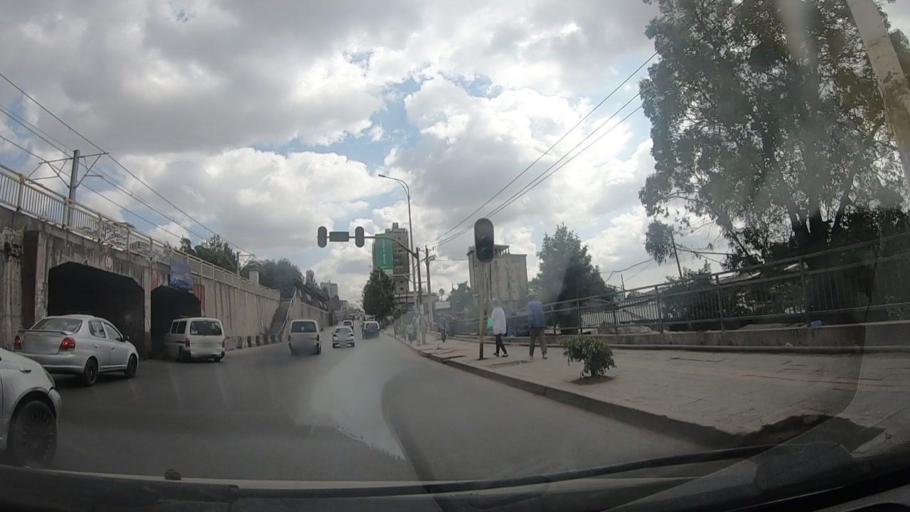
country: ET
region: Adis Abeba
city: Addis Ababa
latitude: 9.0119
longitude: 38.7285
